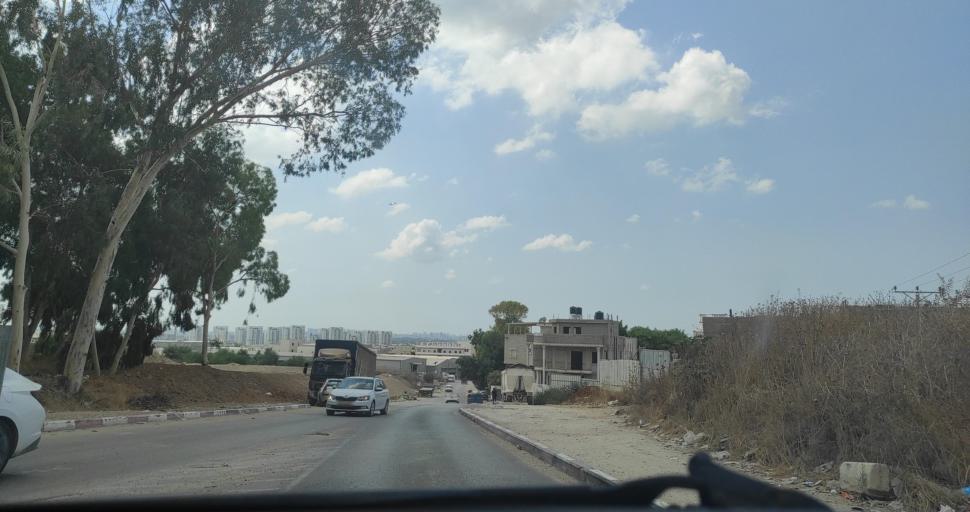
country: IL
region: Central District
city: Kafr Qasim
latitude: 32.1174
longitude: 34.9632
